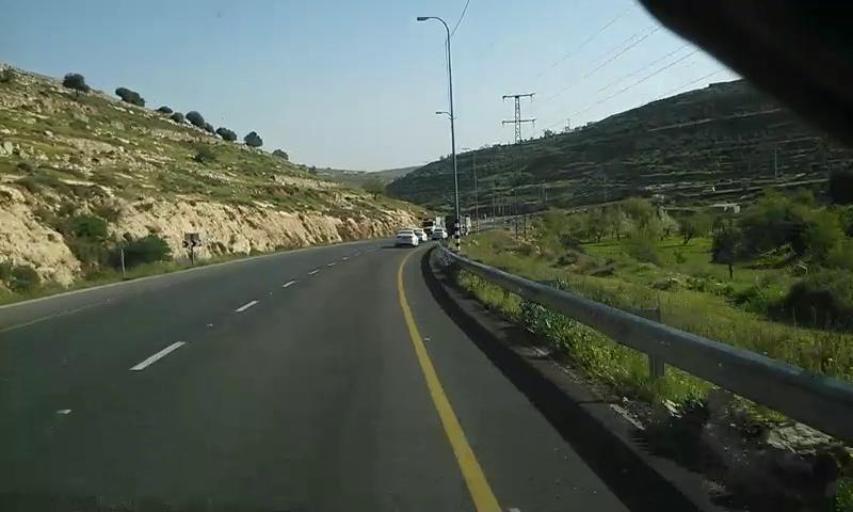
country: PS
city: Al Buq`ah
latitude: 31.5205
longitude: 35.1327
